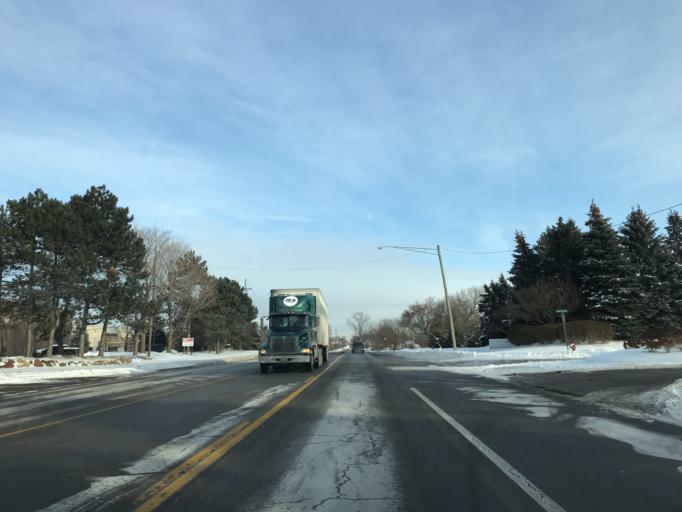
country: US
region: Michigan
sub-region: Oakland County
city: Wixom
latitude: 42.5240
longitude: -83.5473
